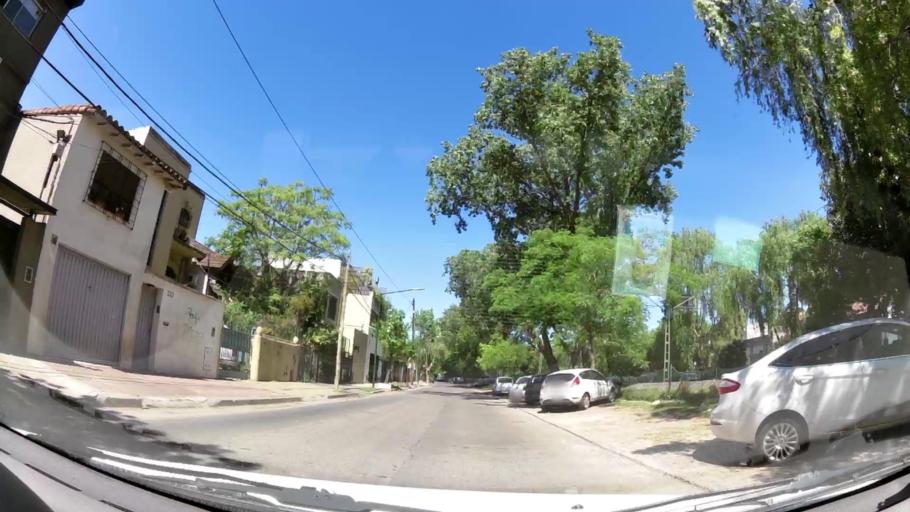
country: AR
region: Buenos Aires
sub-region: Partido de San Isidro
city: San Isidro
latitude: -34.4709
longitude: -58.4979
